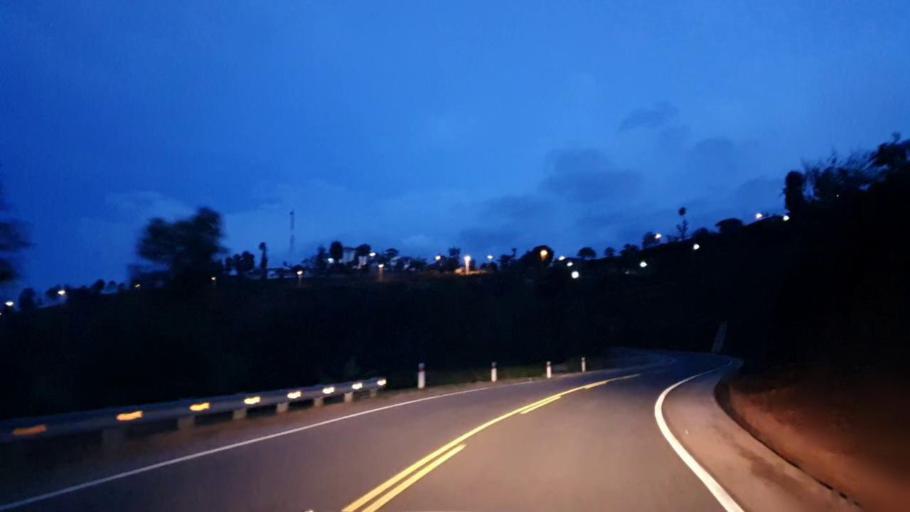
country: RW
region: Southern Province
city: Gikongoro
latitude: -2.4658
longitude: 29.5697
